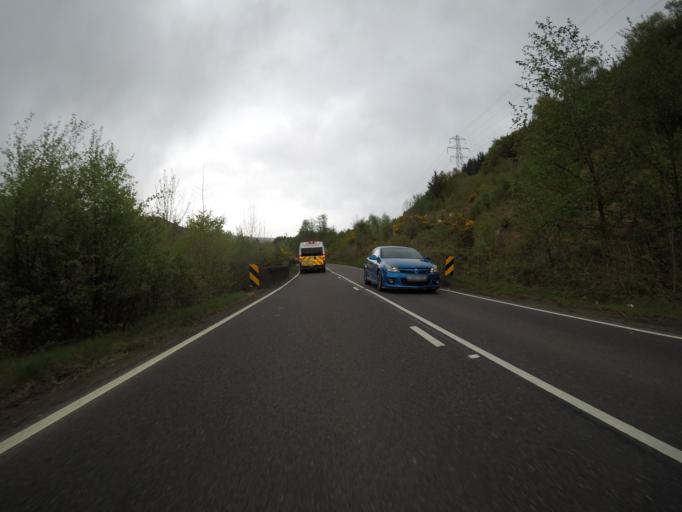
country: GB
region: Scotland
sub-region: Highland
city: Spean Bridge
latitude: 57.0213
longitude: -4.8246
